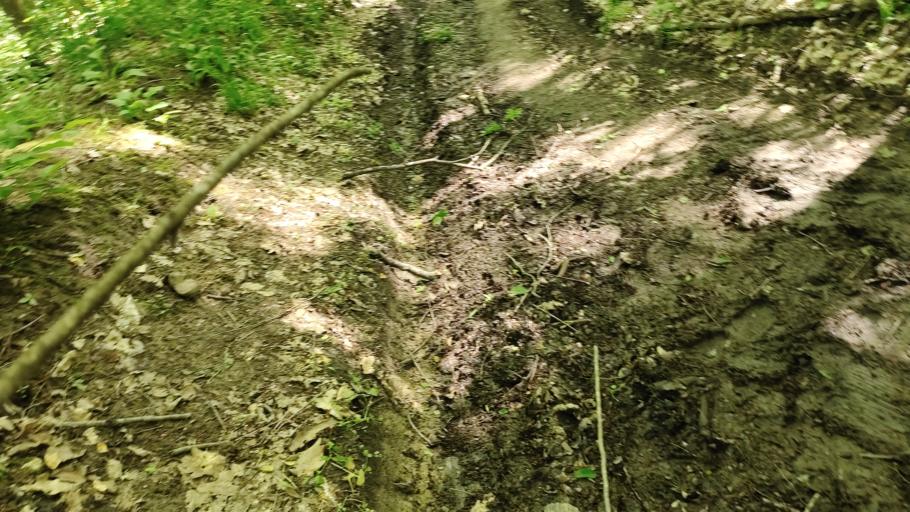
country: RU
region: Krasnodarskiy
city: Goryachiy Klyuch
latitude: 44.6812
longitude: 38.9778
